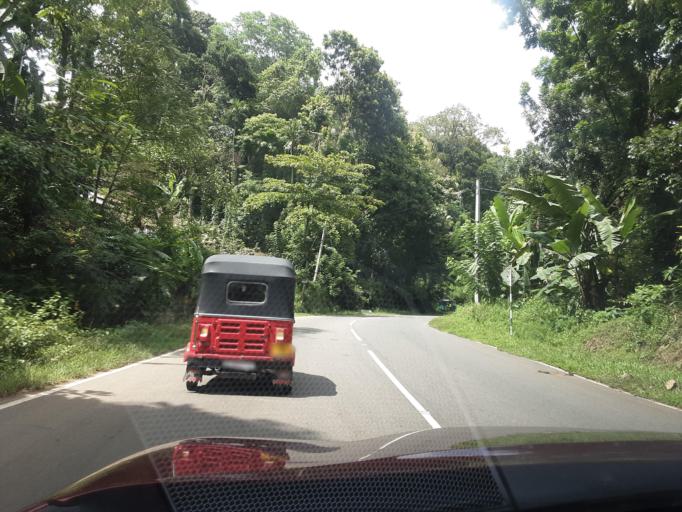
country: LK
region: Uva
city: Monaragala
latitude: 6.8967
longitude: 81.2512
